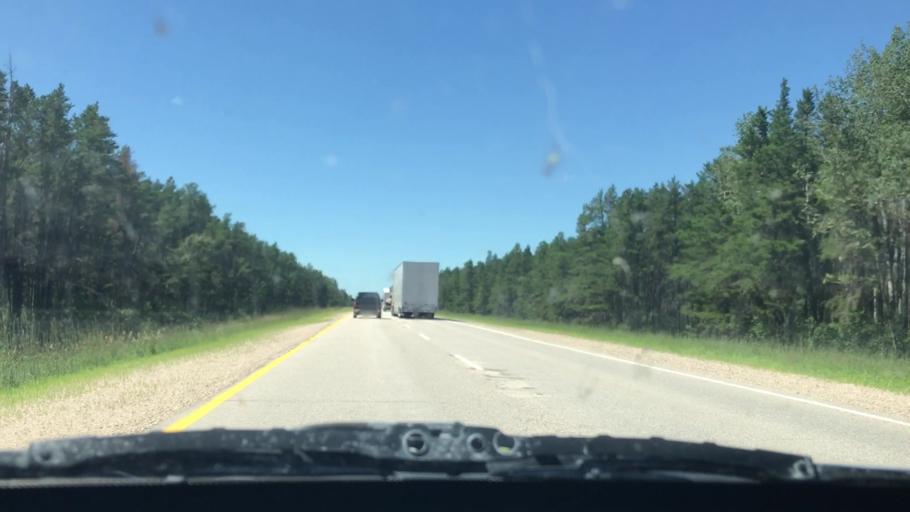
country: CA
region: Manitoba
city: La Broquerie
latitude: 49.6576
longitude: -96.2022
